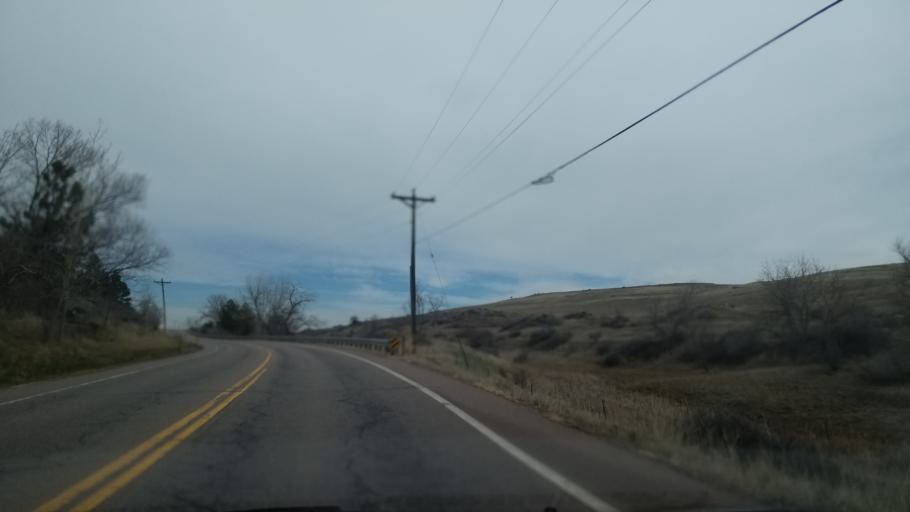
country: US
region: Colorado
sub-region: Boulder County
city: Superior
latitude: 39.9564
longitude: -105.2159
